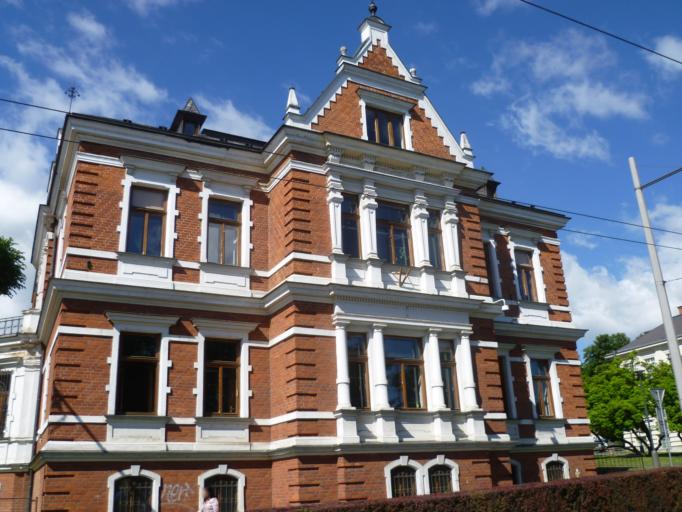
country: CZ
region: Moravskoslezsky
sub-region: Okres Opava
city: Opava
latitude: 49.9344
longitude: 17.9082
